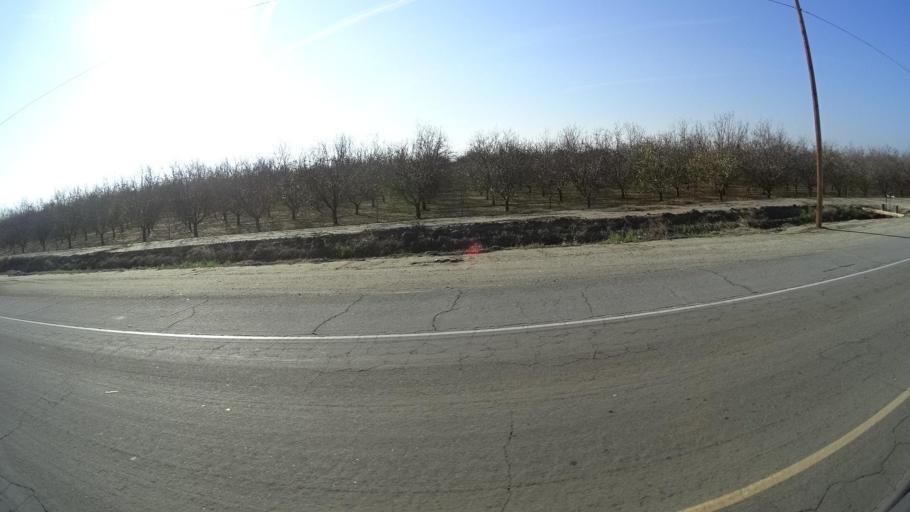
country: US
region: California
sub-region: Kern County
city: Greenfield
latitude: 35.2523
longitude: -118.9939
